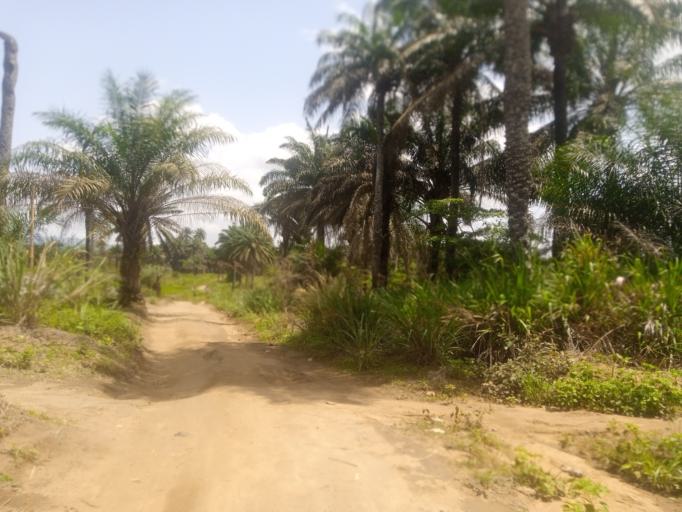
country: SL
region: Western Area
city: Waterloo
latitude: 8.3194
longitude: -13.0084
